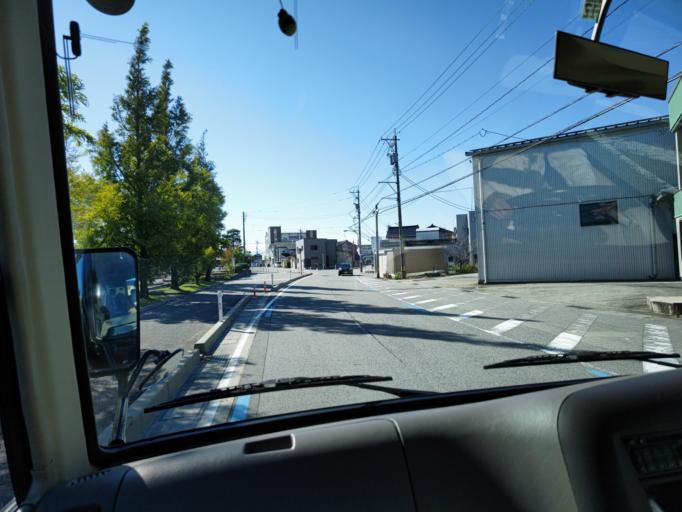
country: JP
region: Toyama
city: Nyuzen
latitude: 36.9072
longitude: 137.4261
